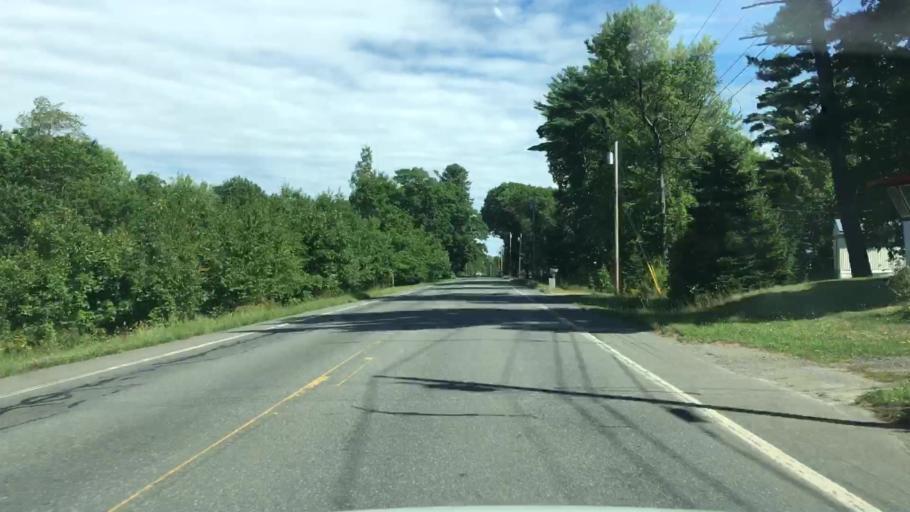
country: US
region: Maine
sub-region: Penobscot County
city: Garland
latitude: 45.0832
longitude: -69.2281
